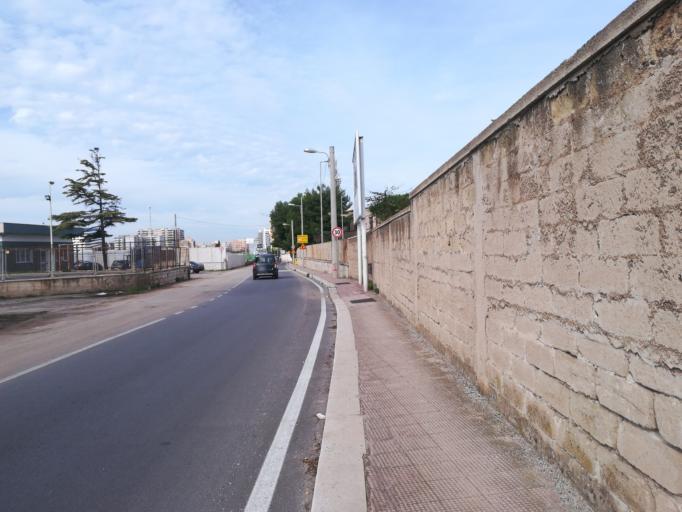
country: IT
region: Apulia
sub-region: Provincia di Bari
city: Bari
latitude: 41.1122
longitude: 16.8886
